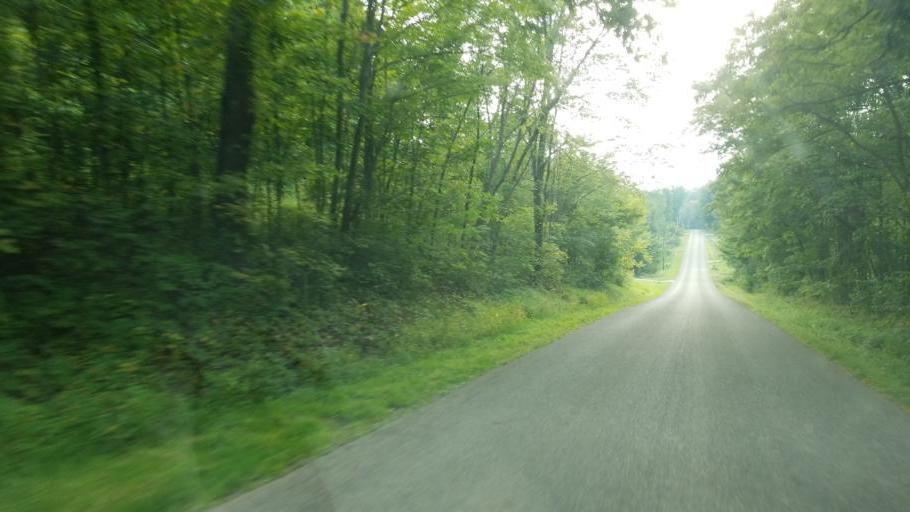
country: US
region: Ohio
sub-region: Sandusky County
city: Bellville
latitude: 40.6415
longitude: -82.5055
